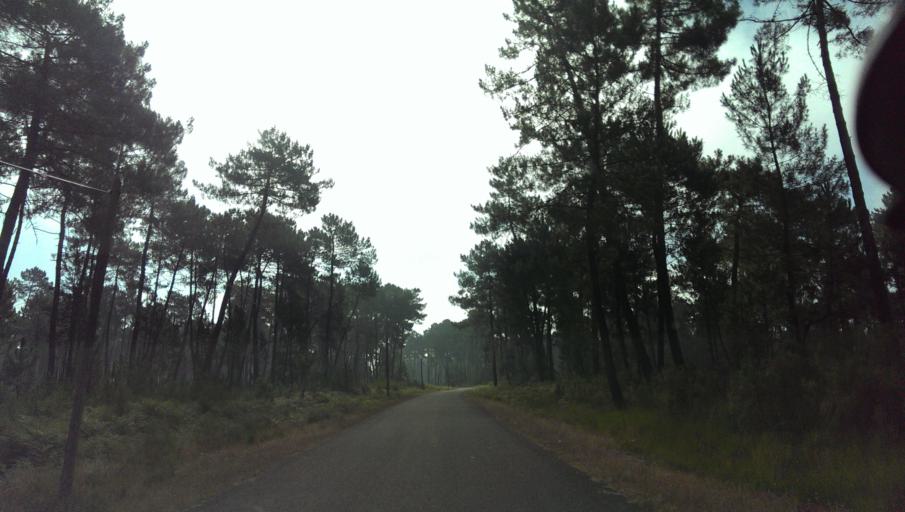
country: FR
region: Aquitaine
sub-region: Departement des Landes
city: Gabarret
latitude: 44.1125
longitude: -0.0707
